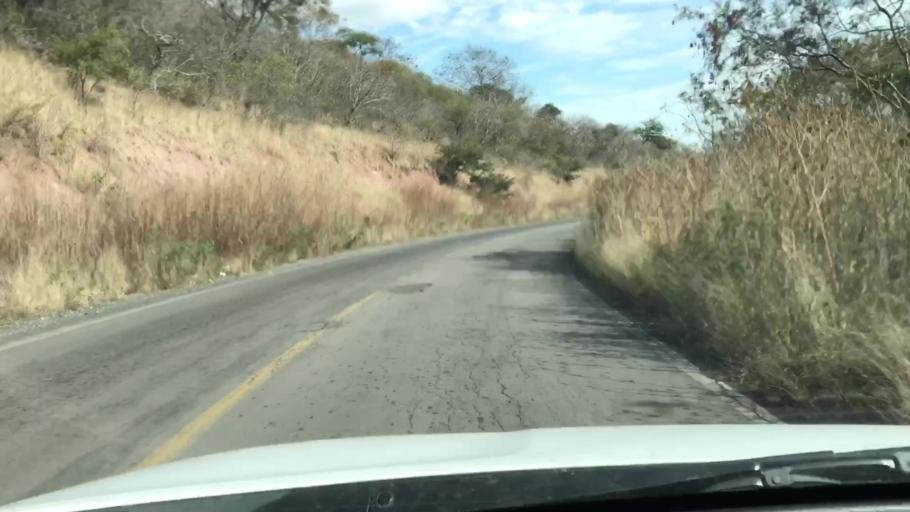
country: MX
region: Jalisco
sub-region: Zacoalco de Torres
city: Barranca de Otates (Barranca de Otatan)
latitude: 20.2454
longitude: -103.6711
